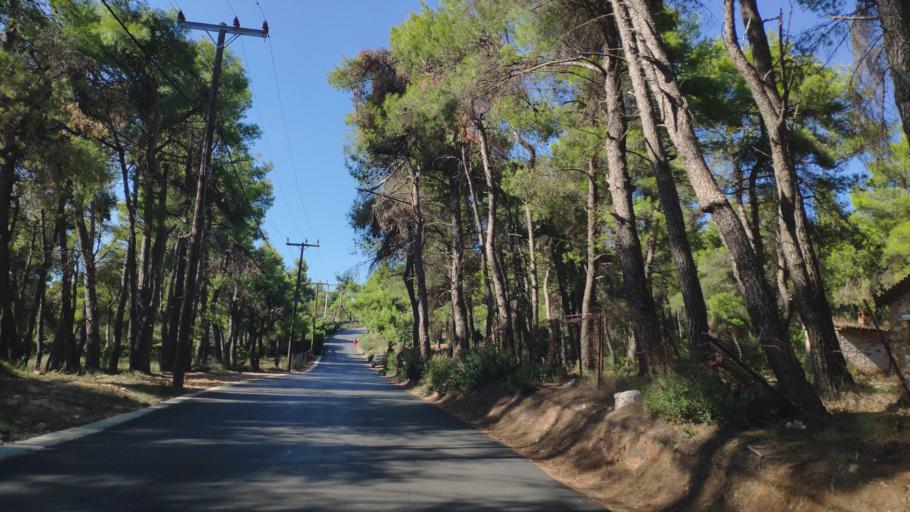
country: GR
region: Attica
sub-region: Nomarchia Anatolikis Attikis
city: Drosia
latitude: 38.1249
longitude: 23.8725
